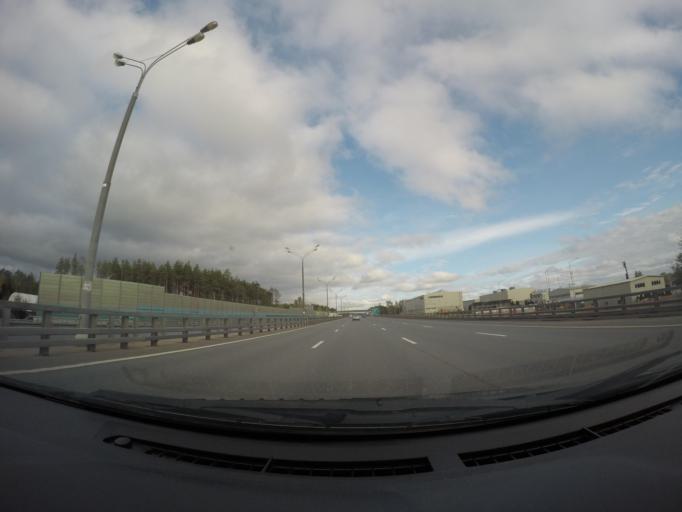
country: RU
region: Moskovskaya
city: Zhavoronki
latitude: 55.6131
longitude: 37.0806
